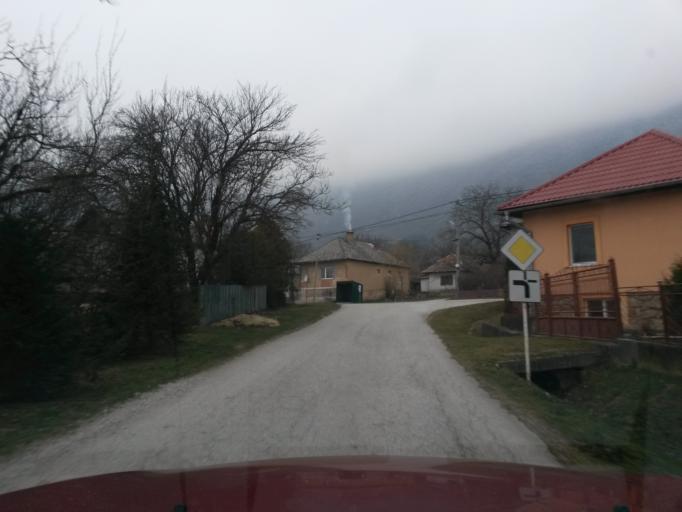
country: SK
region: Kosicky
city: Medzev
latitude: 48.6047
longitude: 20.7562
